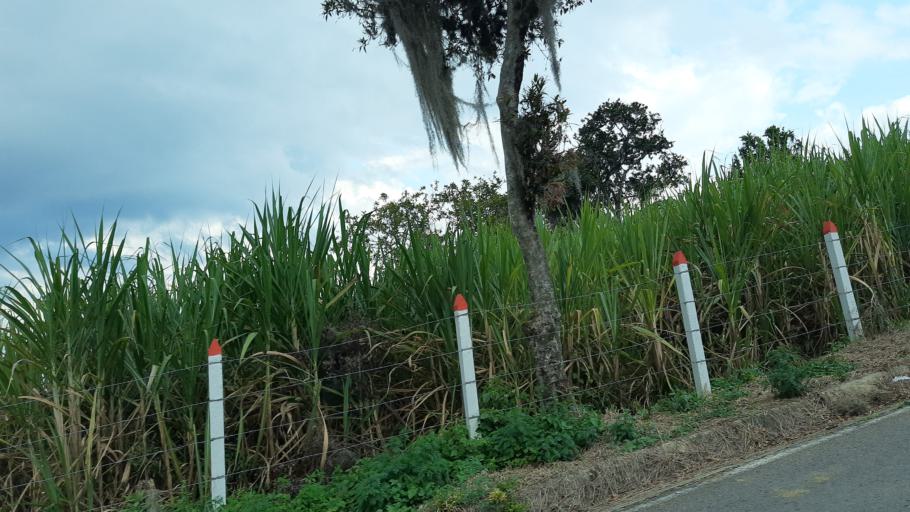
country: CO
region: Boyaca
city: Moniquira
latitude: 5.8154
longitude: -73.5994
